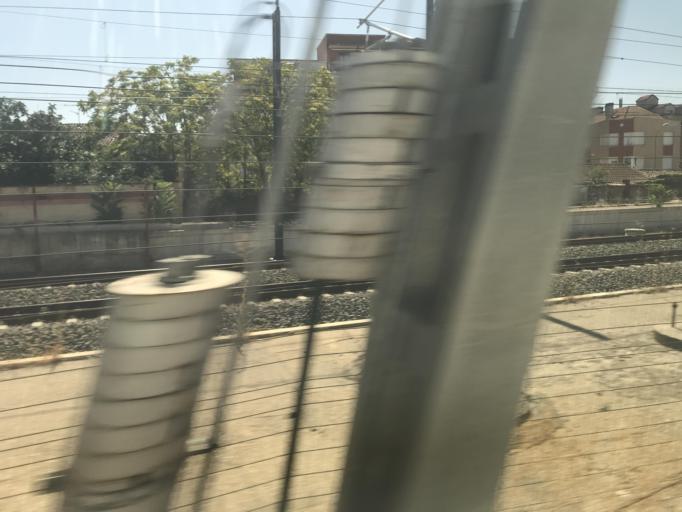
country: ES
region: Castille and Leon
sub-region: Provincia de Palencia
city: Venta de Banos
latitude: 41.9197
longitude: -4.4935
